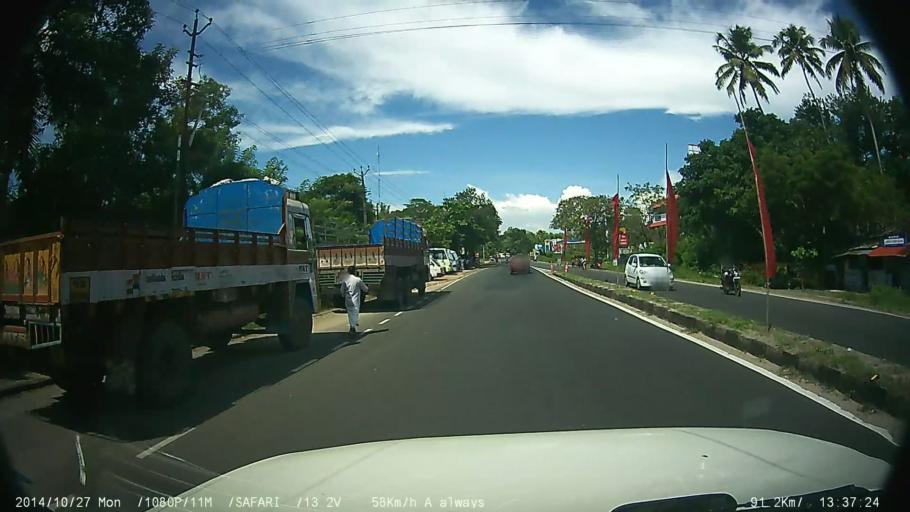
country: IN
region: Kerala
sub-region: Alappuzha
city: Shertallai
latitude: 9.6103
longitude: 76.3298
